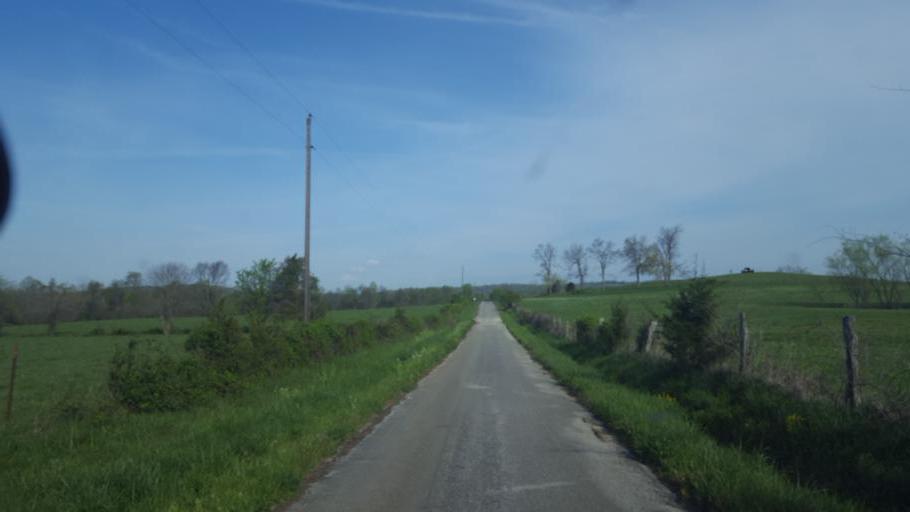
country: US
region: Kentucky
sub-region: Edmonson County
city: Brownsville
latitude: 37.3301
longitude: -86.1104
